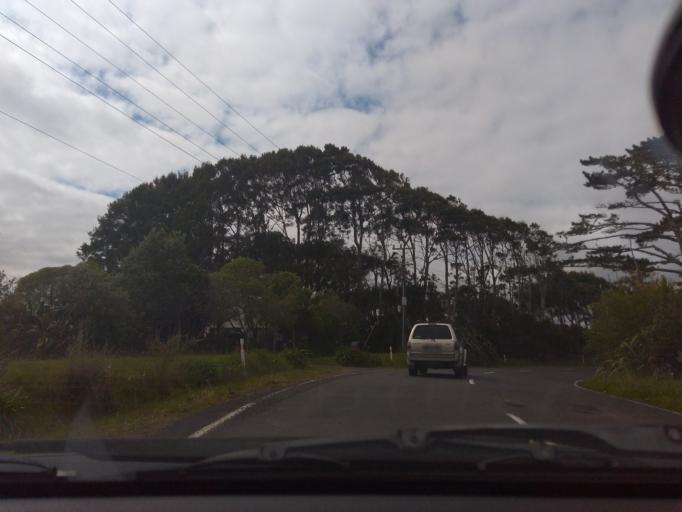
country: NZ
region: Auckland
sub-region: Auckland
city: Muriwai Beach
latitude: -36.8503
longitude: 174.5125
